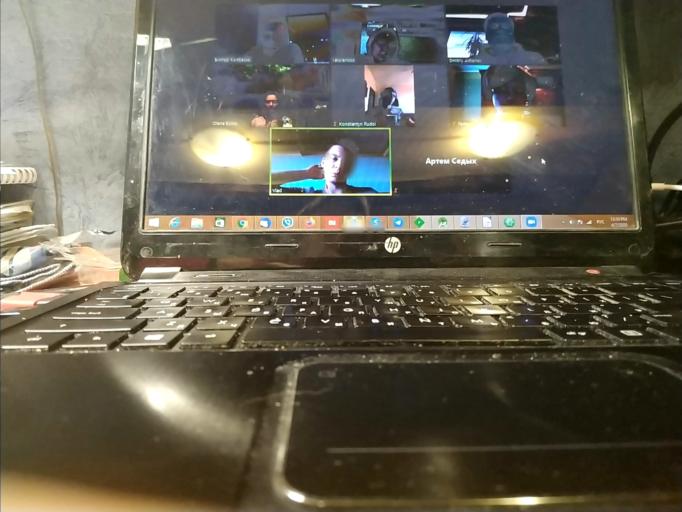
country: RU
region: Tverskaya
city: Ves'yegonsk
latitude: 58.7005
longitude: 37.5439
